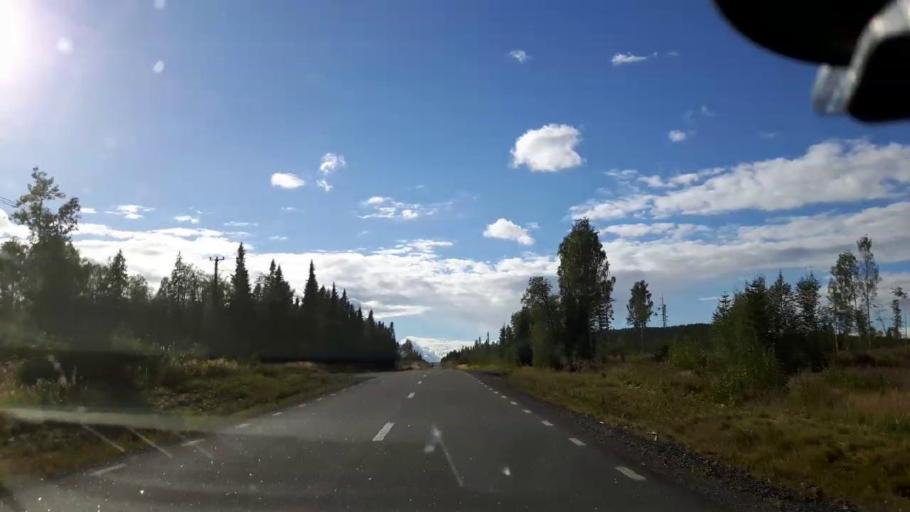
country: SE
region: Jaemtland
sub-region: Stroemsunds Kommun
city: Stroemsund
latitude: 63.5415
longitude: 15.9538
